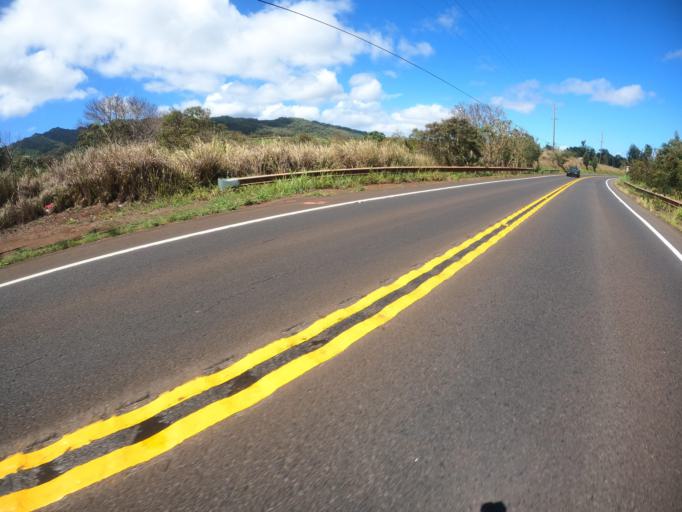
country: US
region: Hawaii
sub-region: Honolulu County
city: Schofield Barracks
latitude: 21.4517
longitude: -158.0602
